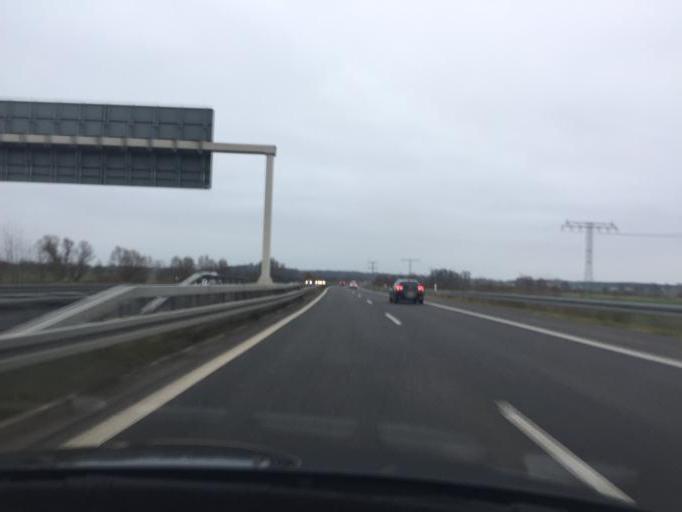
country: DE
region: Brandenburg
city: Rangsdorf
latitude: 52.3396
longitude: 13.4446
